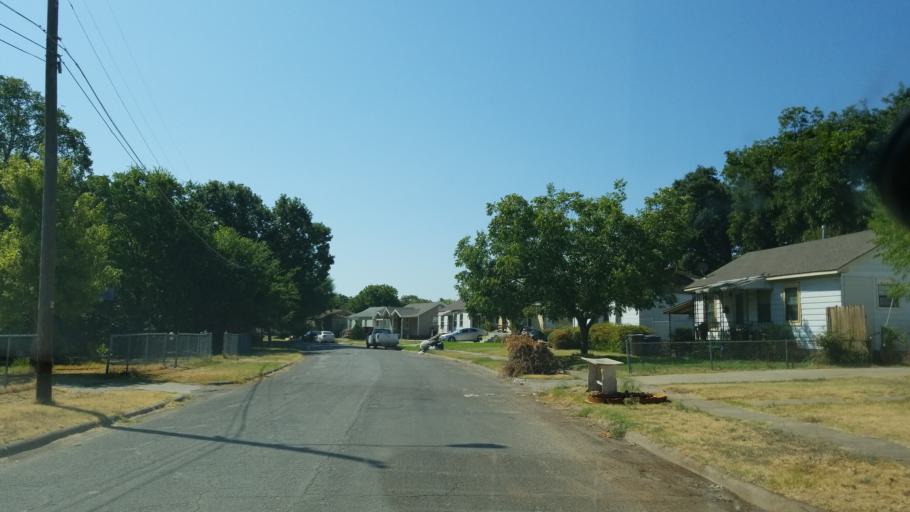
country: US
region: Texas
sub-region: Dallas County
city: Cockrell Hill
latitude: 32.7464
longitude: -96.8882
